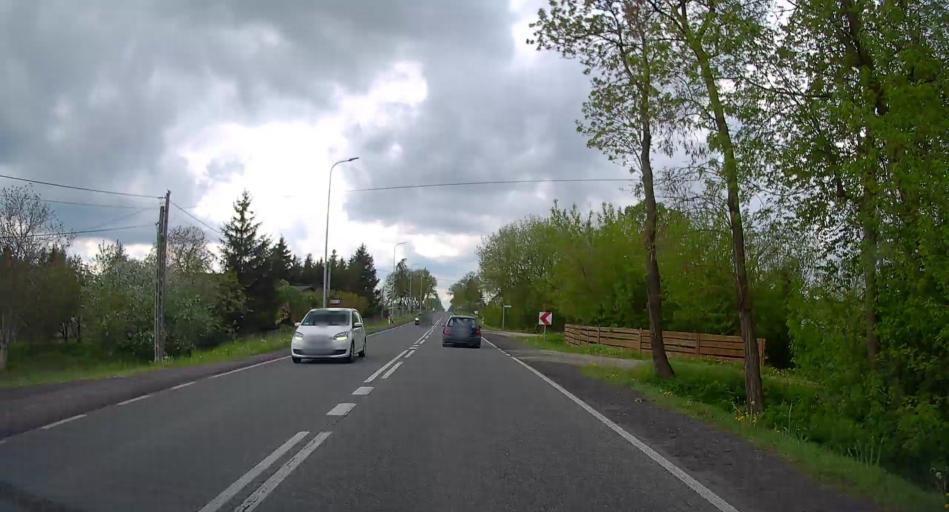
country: PL
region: Masovian Voivodeship
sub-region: Powiat plonski
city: Zaluski
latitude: 52.4463
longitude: 20.4987
